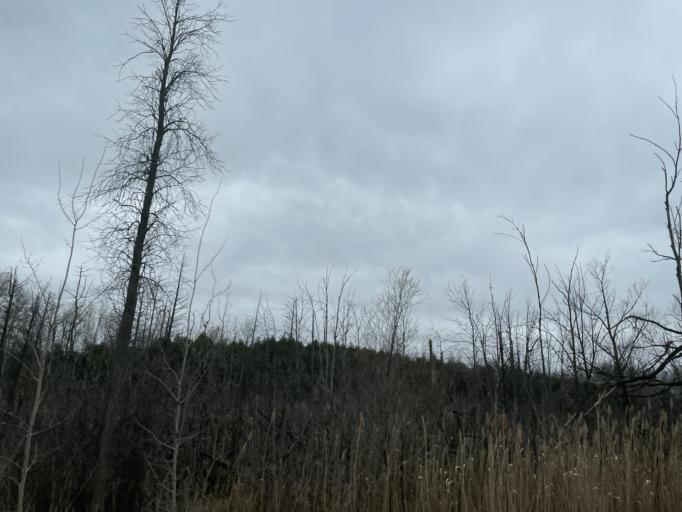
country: CA
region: Ontario
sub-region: Wellington County
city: Guelph
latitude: 43.5751
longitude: -80.2202
